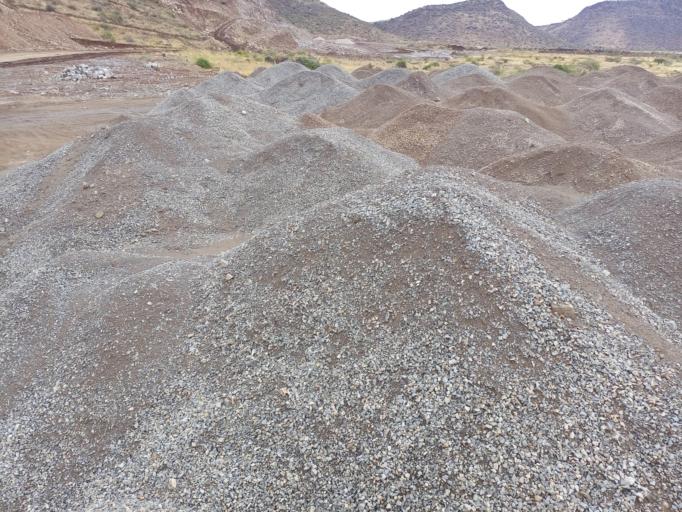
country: ET
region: Oromiya
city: Ziway
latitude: 7.9371
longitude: 38.6157
